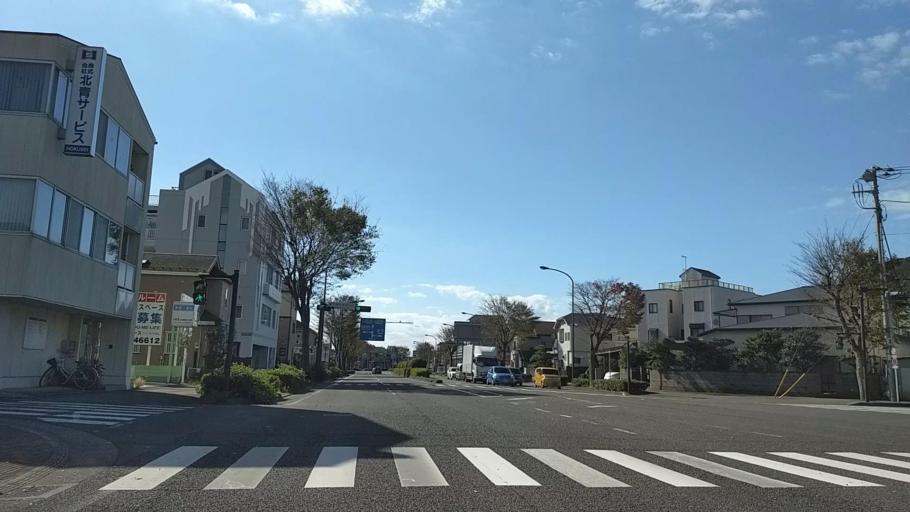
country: JP
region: Kanagawa
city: Hiratsuka
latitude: 35.3276
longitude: 139.3332
